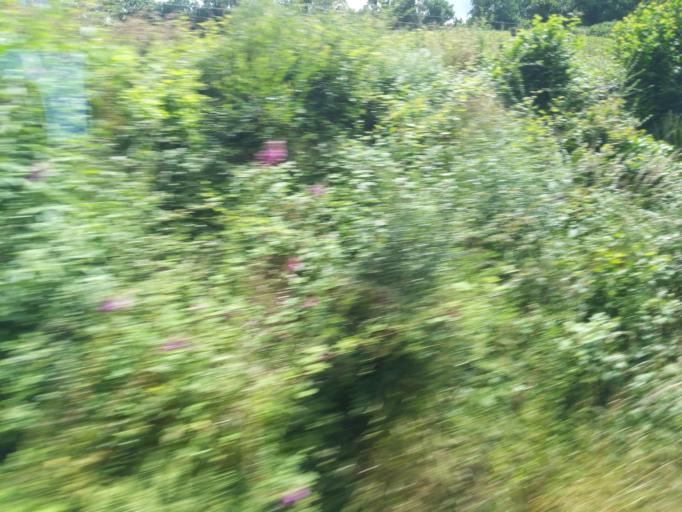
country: GB
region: England
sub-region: Cornwall
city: Par
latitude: 50.3644
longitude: -4.6889
